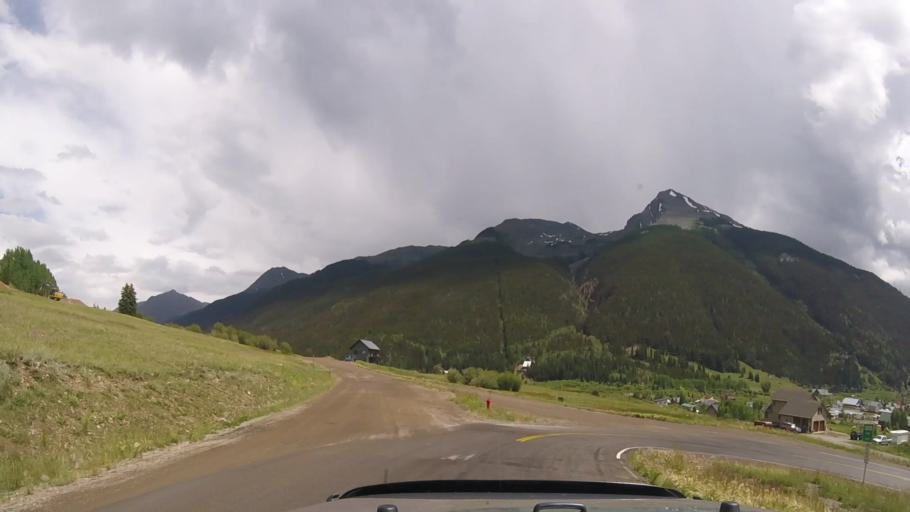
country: US
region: Colorado
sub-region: San Juan County
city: Silverton
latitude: 37.8185
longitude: -107.6585
